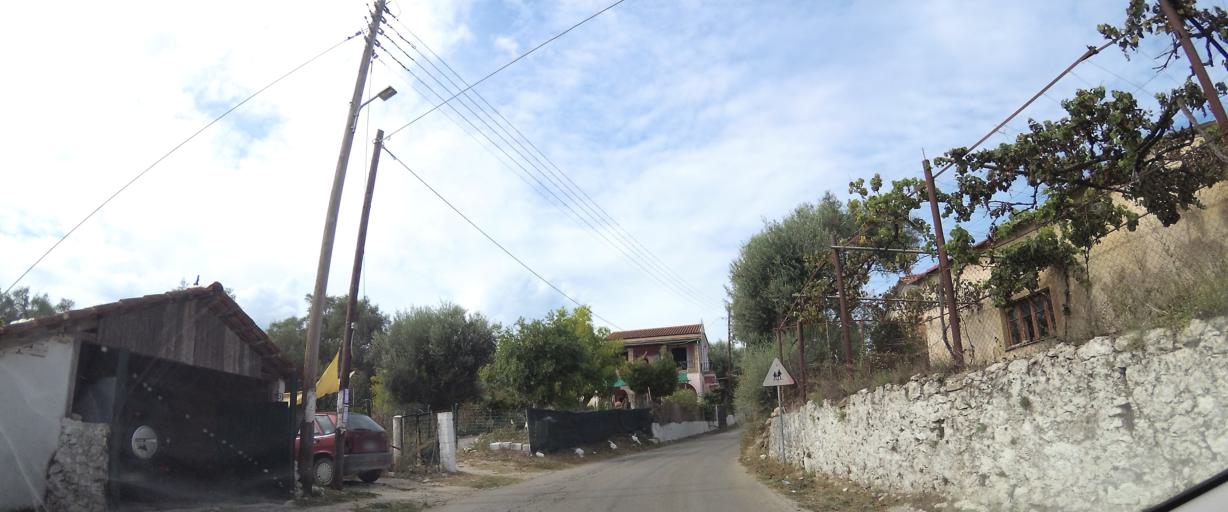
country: GR
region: Ionian Islands
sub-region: Nomos Kerkyras
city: Kontokali
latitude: 39.6902
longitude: 19.8259
